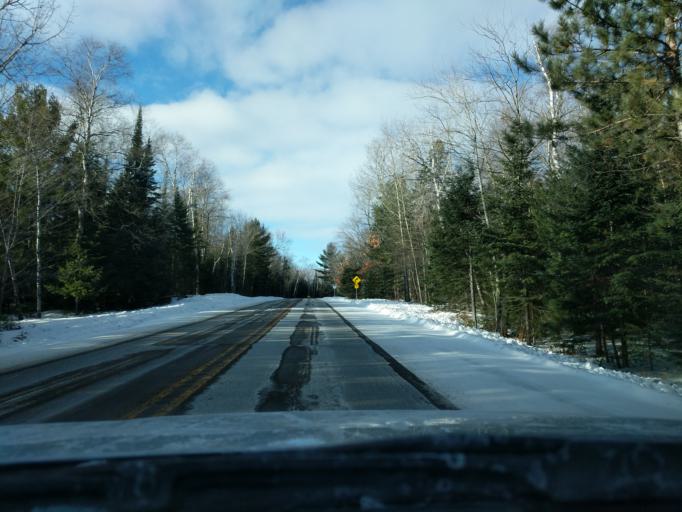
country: US
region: Wisconsin
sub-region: Vilas County
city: Eagle River
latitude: 45.7640
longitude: -89.0664
